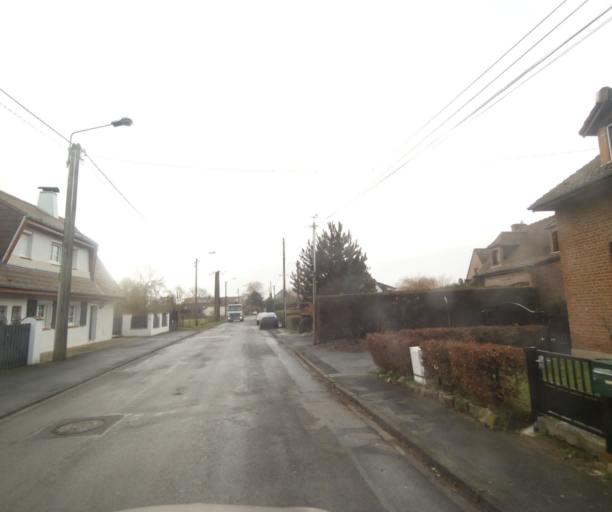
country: FR
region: Nord-Pas-de-Calais
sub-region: Departement du Nord
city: Famars
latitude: 50.3244
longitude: 3.5272
